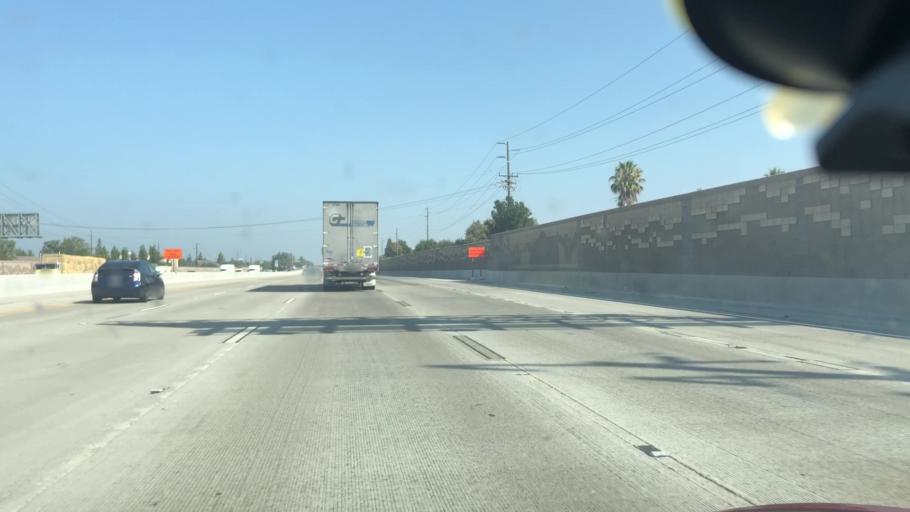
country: US
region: California
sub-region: San Joaquin County
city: Lincoln Village
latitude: 38.0134
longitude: -121.3547
